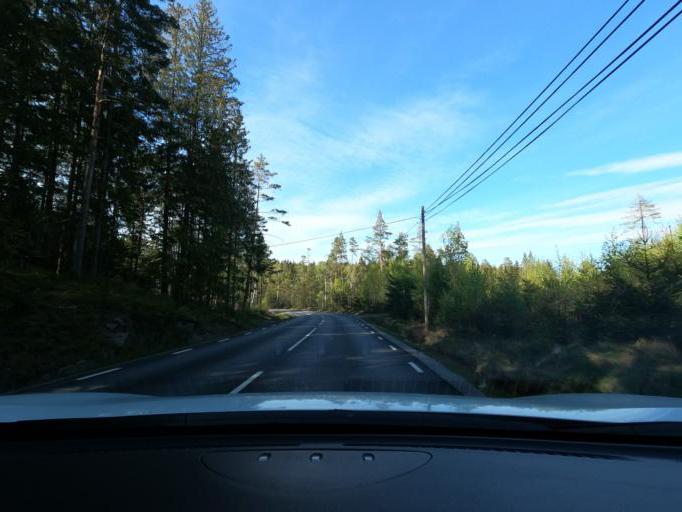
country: SE
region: Vaestra Goetaland
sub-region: Harryda Kommun
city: Landvetter
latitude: 57.6226
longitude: 12.2780
